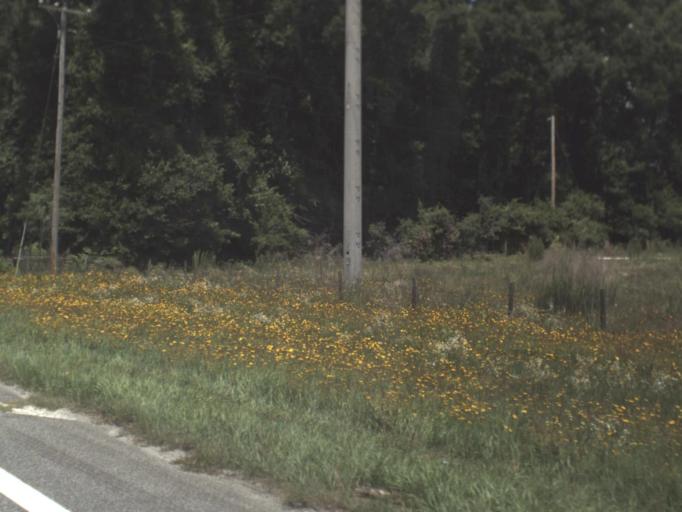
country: US
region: Florida
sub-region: Alachua County
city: High Springs
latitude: 29.9518
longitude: -82.7819
